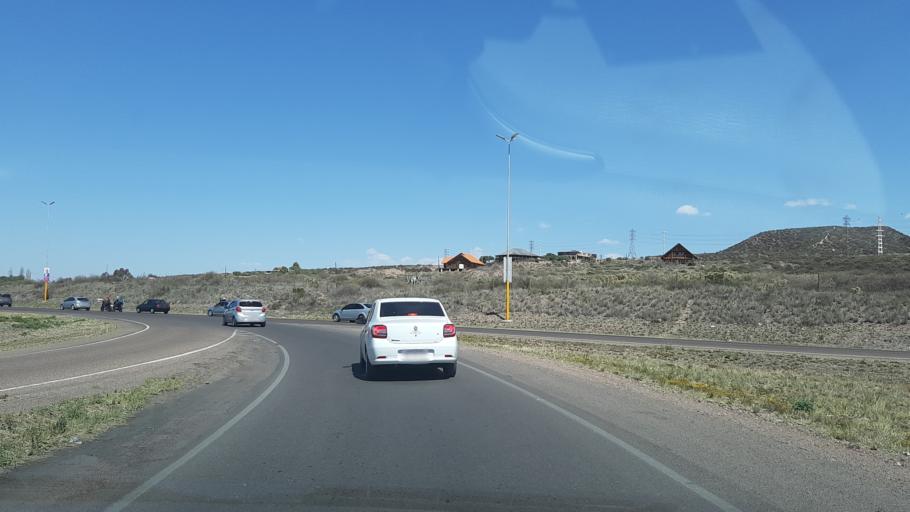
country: AR
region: Mendoza
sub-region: Departamento de Godoy Cruz
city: Godoy Cruz
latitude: -32.9698
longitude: -68.8812
